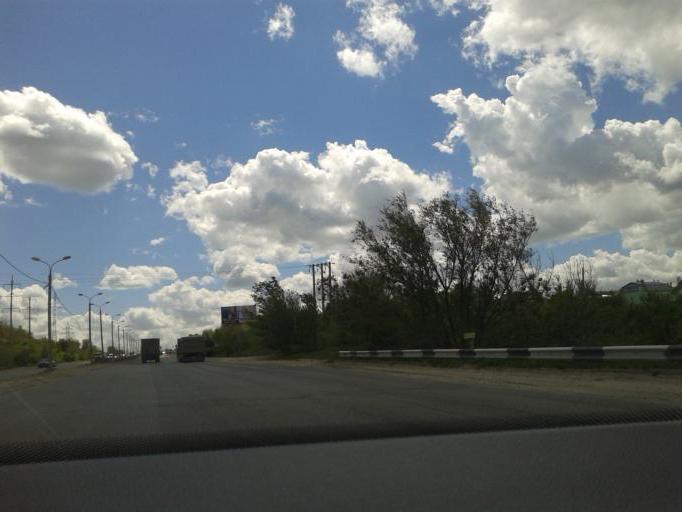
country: RU
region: Volgograd
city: Volgograd
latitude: 48.7120
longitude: 44.4427
